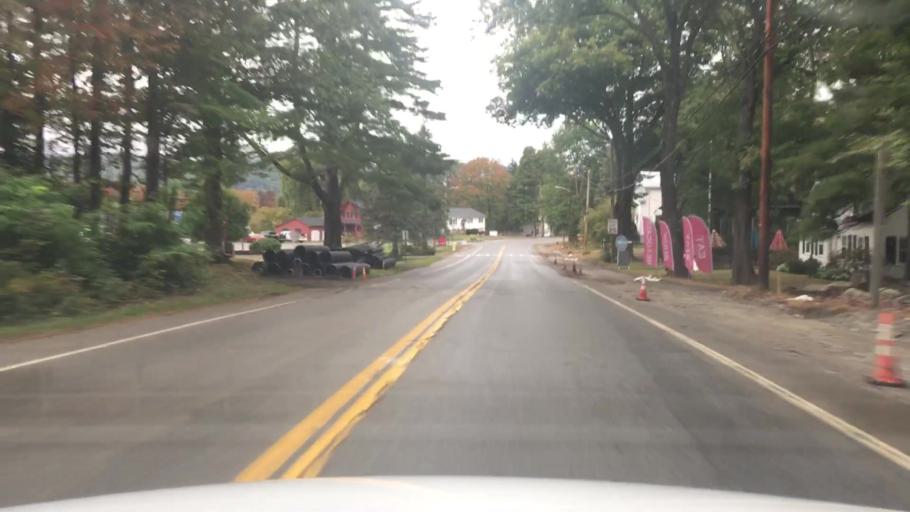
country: US
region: Maine
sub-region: Kennebec County
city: Rome
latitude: 44.5239
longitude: -69.8845
